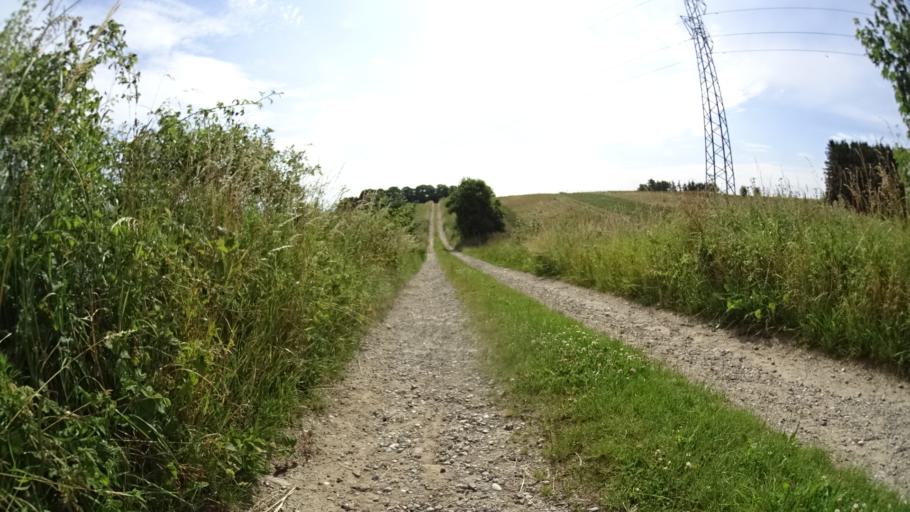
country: DK
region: Central Jutland
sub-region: Arhus Kommune
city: Kolt
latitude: 56.1242
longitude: 10.0751
